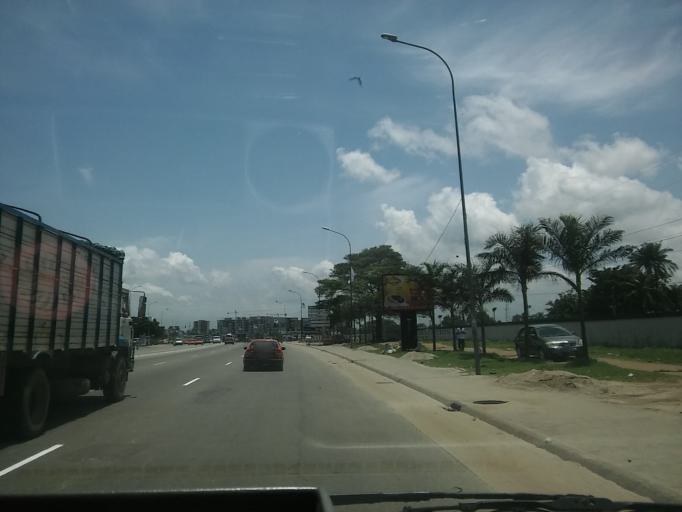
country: CI
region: Lagunes
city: Abidjan
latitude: 5.2585
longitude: -3.9711
